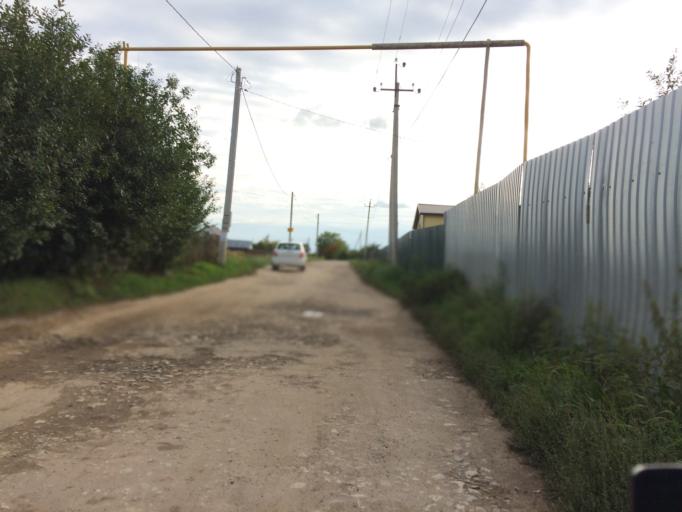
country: RU
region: Mariy-El
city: Yoshkar-Ola
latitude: 56.6566
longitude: 48.0056
